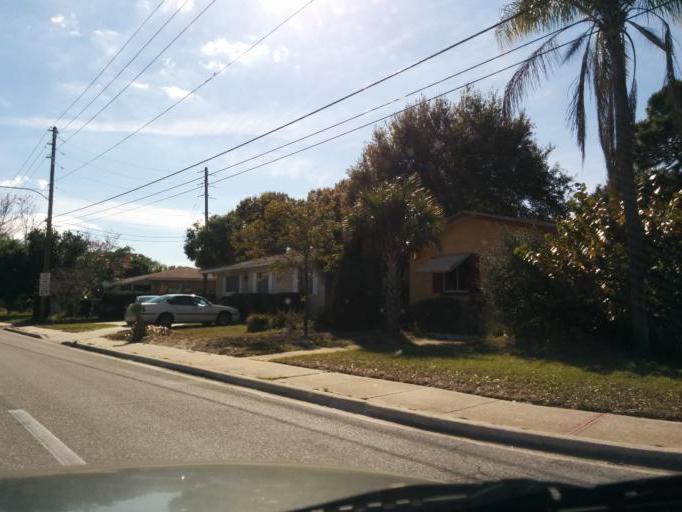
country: US
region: Florida
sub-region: Pinellas County
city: Lealman
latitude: 27.8030
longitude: -82.6345
